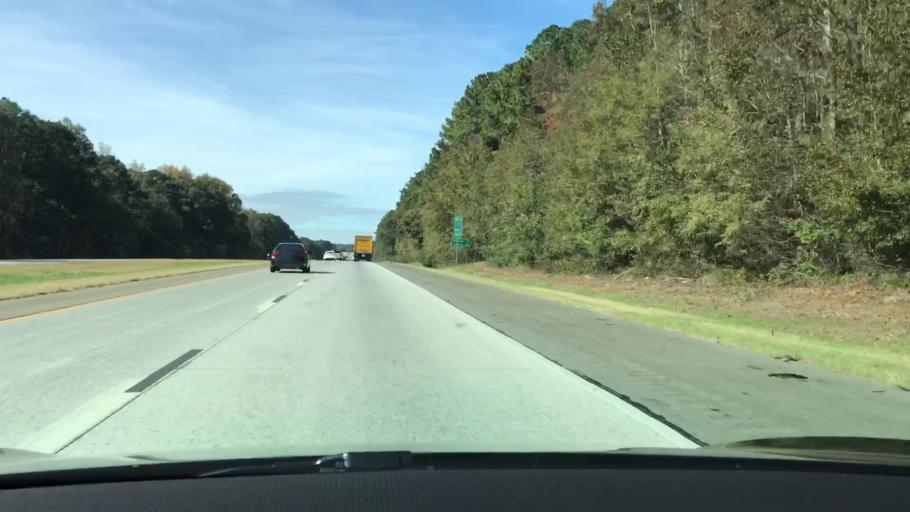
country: US
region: Georgia
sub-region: Morgan County
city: Madison
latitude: 33.5553
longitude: -83.3777
